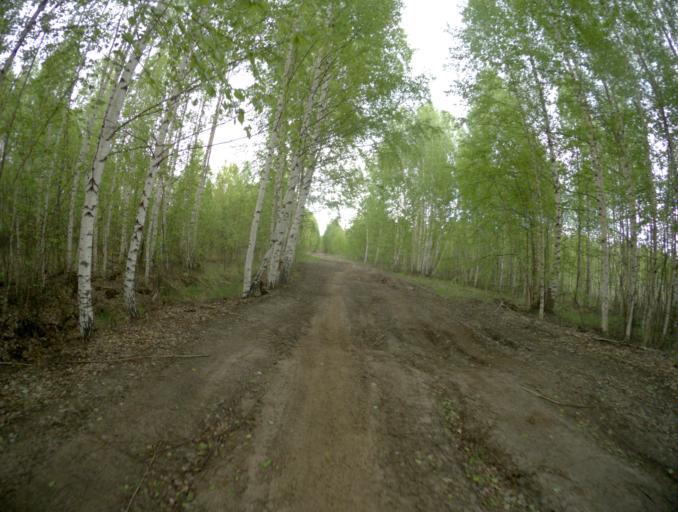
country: RU
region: Vladimir
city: Urshel'skiy
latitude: 55.5953
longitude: 40.1356
